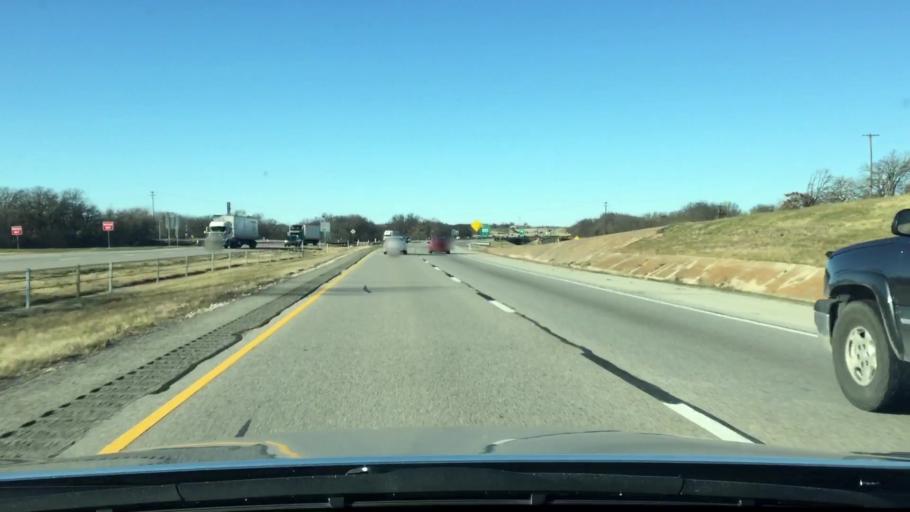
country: US
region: Texas
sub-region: Johnson County
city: Grandview
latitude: 32.2876
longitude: -97.1778
